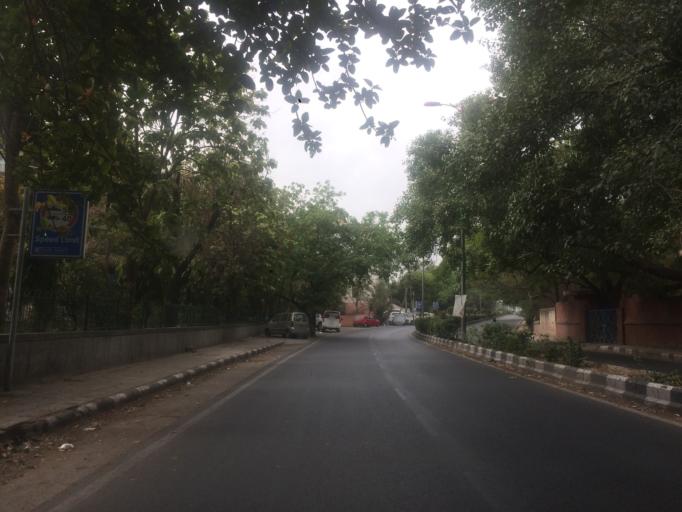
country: IN
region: NCT
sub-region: Central Delhi
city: Karol Bagh
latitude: 28.6315
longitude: 77.1753
